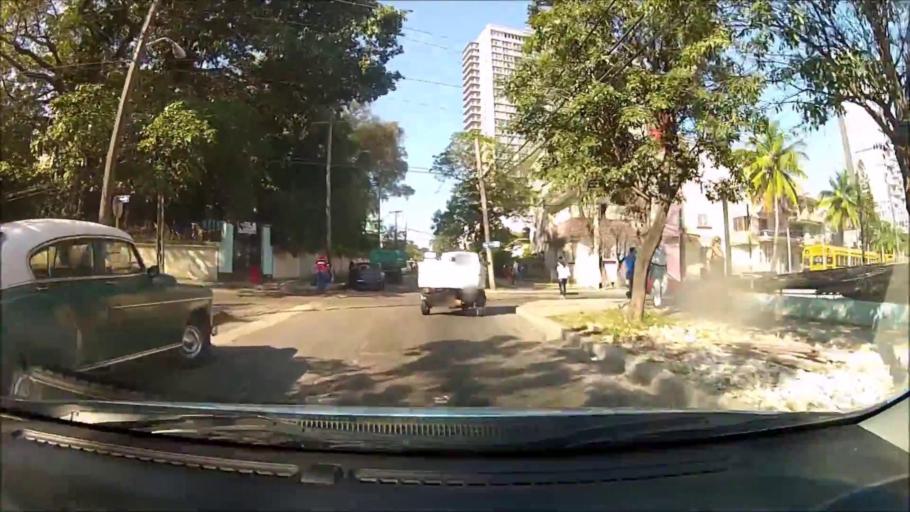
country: CU
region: La Habana
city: Havana
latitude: 23.1399
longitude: -82.3806
